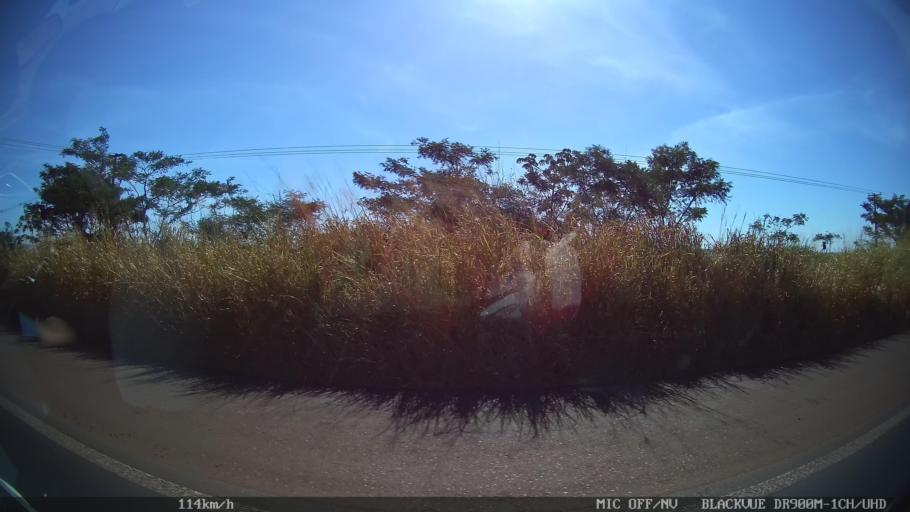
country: BR
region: Sao Paulo
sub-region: Barretos
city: Barretos
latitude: -20.4793
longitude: -48.5012
